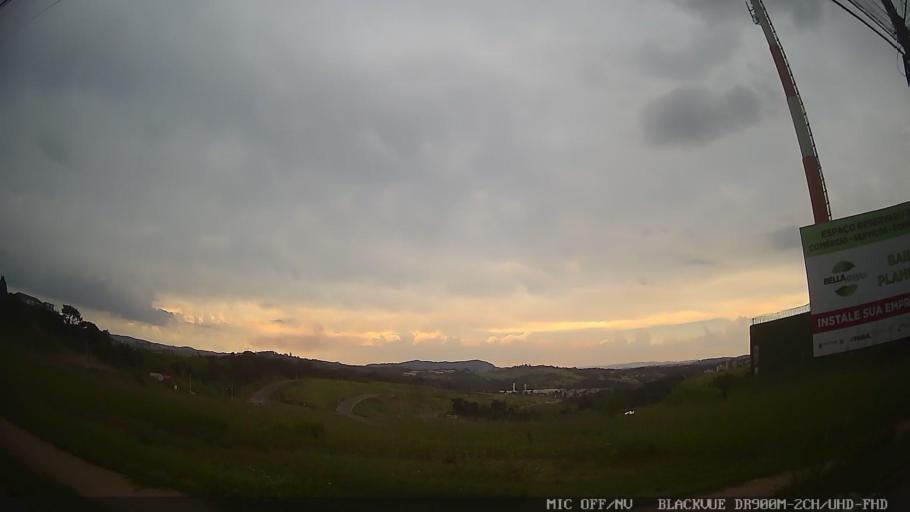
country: BR
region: Sao Paulo
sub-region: Atibaia
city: Atibaia
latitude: -23.1388
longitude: -46.5891
